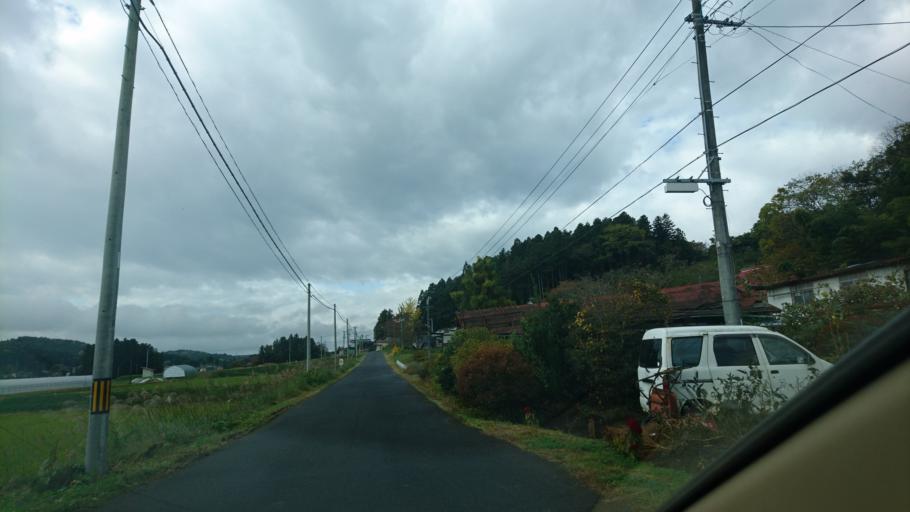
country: JP
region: Iwate
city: Ichinoseki
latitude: 38.7767
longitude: 141.0081
